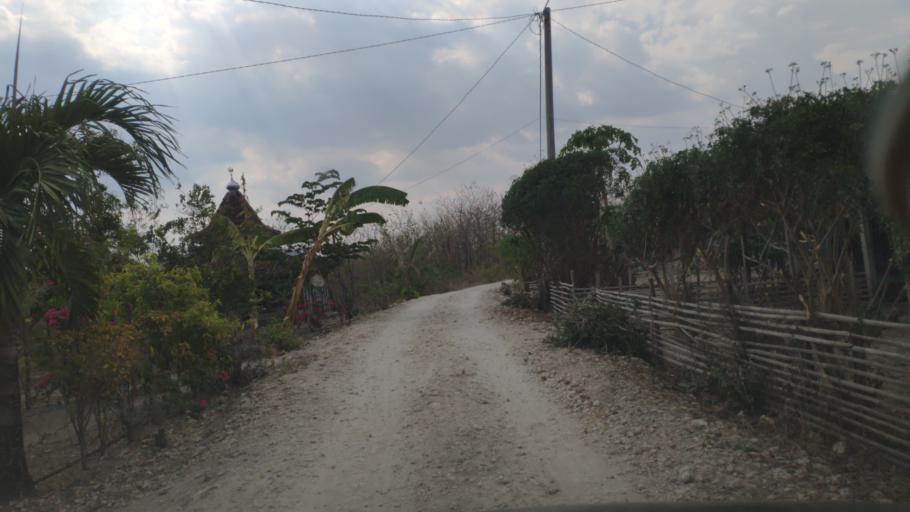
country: ID
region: Central Java
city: Randublatung
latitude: -7.3010
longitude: 111.3378
